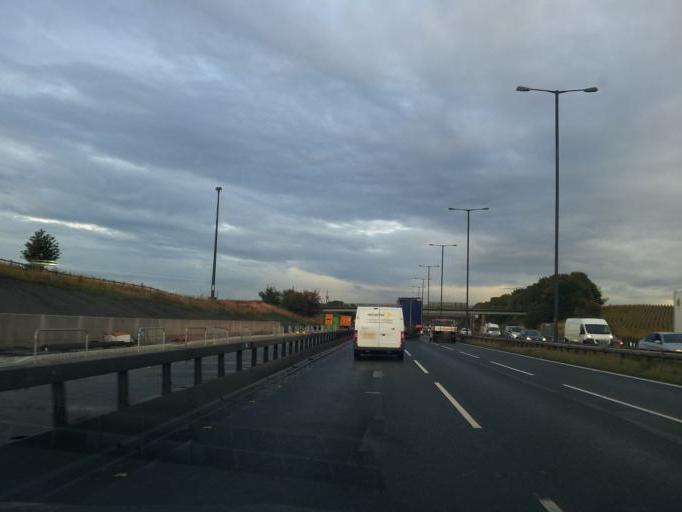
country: GB
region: England
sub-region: Manchester
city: Crumpsall
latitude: 53.5579
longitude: -2.2471
